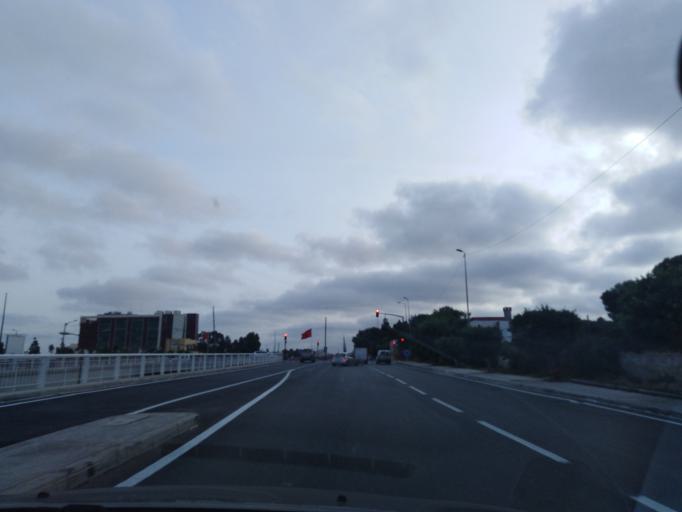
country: MA
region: Grand Casablanca
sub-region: Casablanca
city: Casablanca
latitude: 33.5444
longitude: -7.6524
